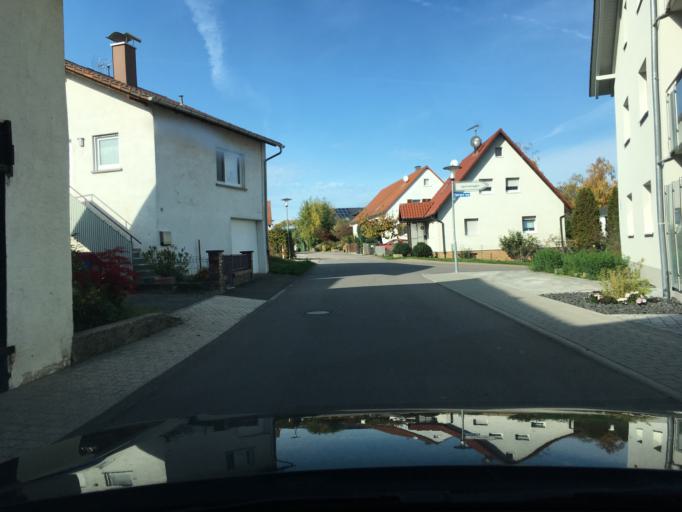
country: DE
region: Baden-Wuerttemberg
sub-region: Regierungsbezirk Stuttgart
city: Siegelsbach
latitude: 49.2429
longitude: 9.0563
